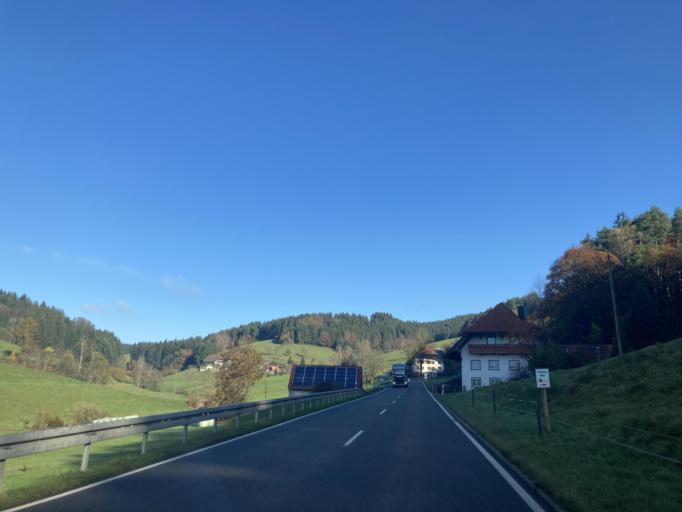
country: DE
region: Baden-Wuerttemberg
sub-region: Freiburg Region
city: Elzach
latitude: 48.2032
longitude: 8.0859
